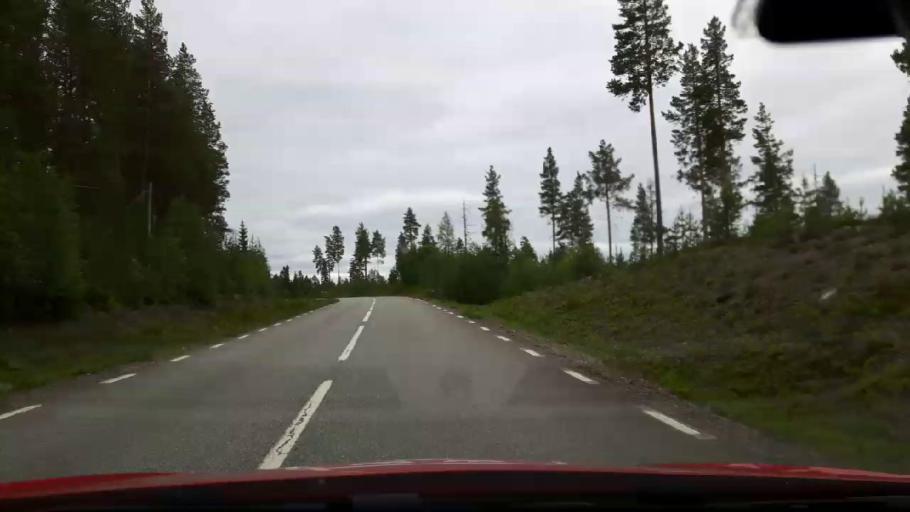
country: SE
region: Jaemtland
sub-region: Stroemsunds Kommun
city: Stroemsund
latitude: 63.3811
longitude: 15.6859
